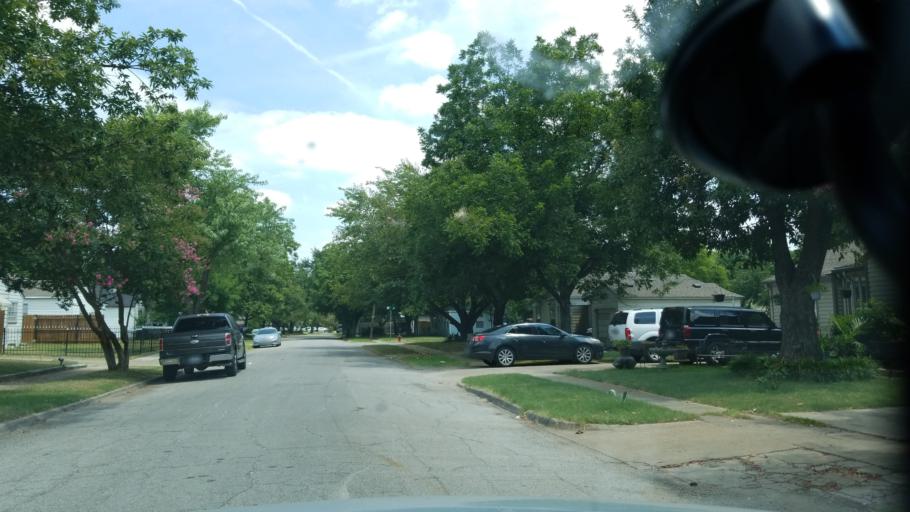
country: US
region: Texas
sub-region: Dallas County
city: Grand Prairie
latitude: 32.7520
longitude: -96.9908
